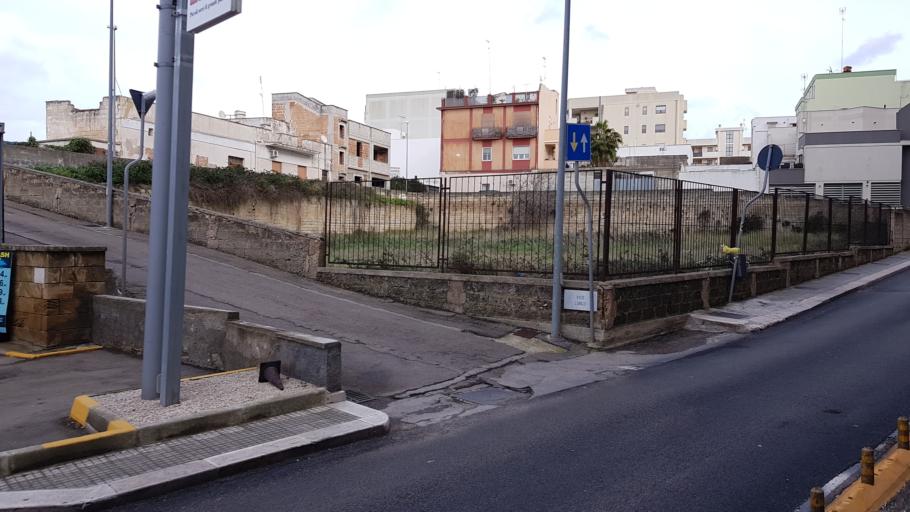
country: IT
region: Apulia
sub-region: Provincia di Brindisi
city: Brindisi
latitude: 40.6377
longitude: 17.9291
